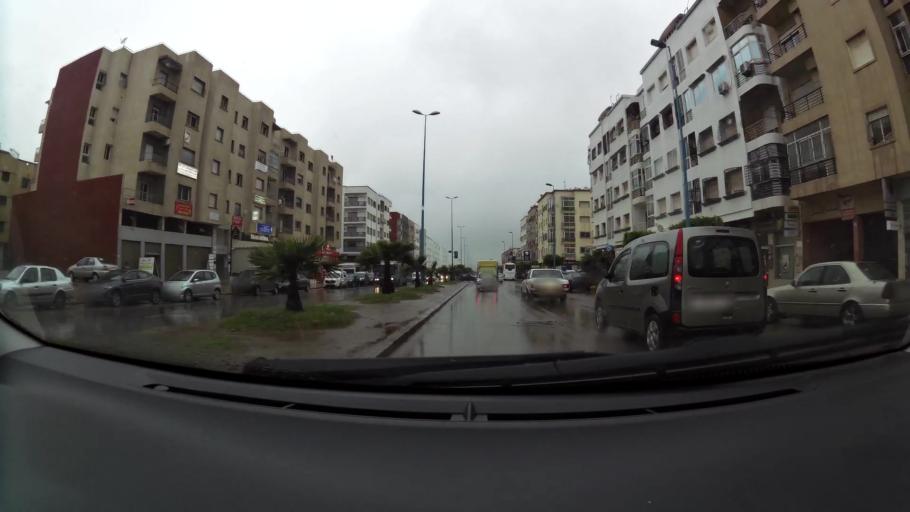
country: MA
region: Grand Casablanca
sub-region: Mediouna
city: Tit Mellil
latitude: 33.5937
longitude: -7.4987
